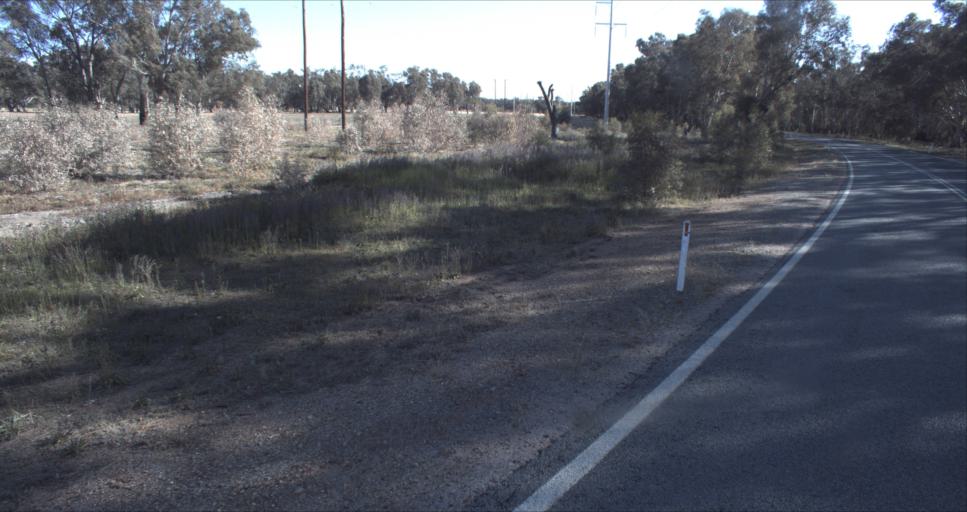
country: AU
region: New South Wales
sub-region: Leeton
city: Leeton
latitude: -34.6239
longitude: 146.3818
